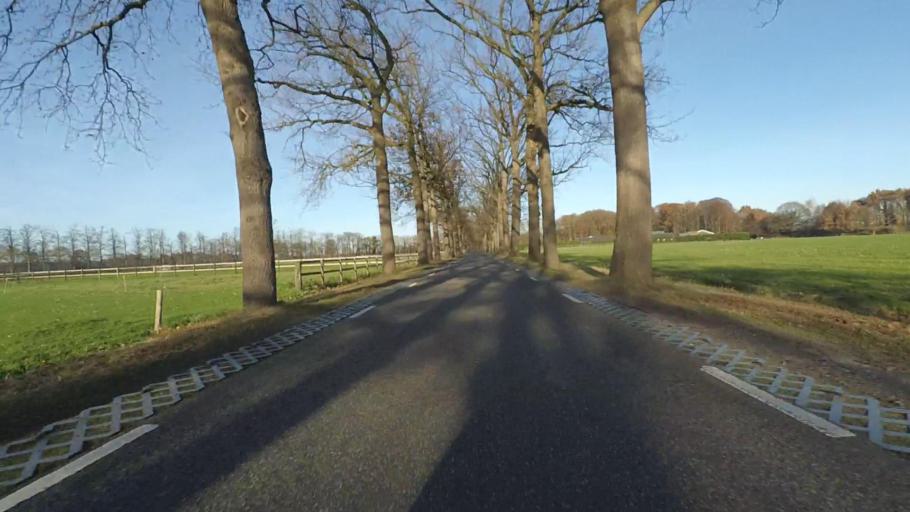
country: NL
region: Utrecht
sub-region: Gemeente Utrechtse Heuvelrug
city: Overberg
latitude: 52.0644
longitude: 5.4750
